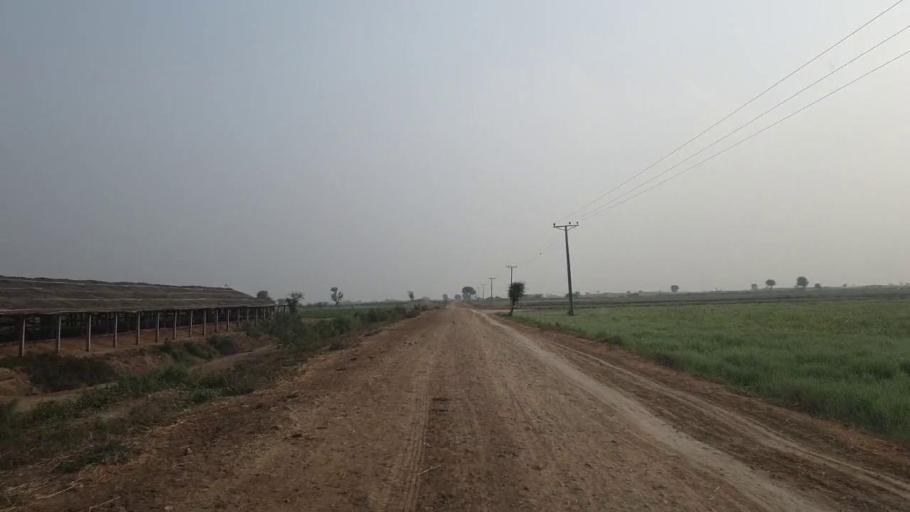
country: PK
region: Sindh
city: Mirpur Batoro
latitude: 24.5512
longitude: 68.4207
